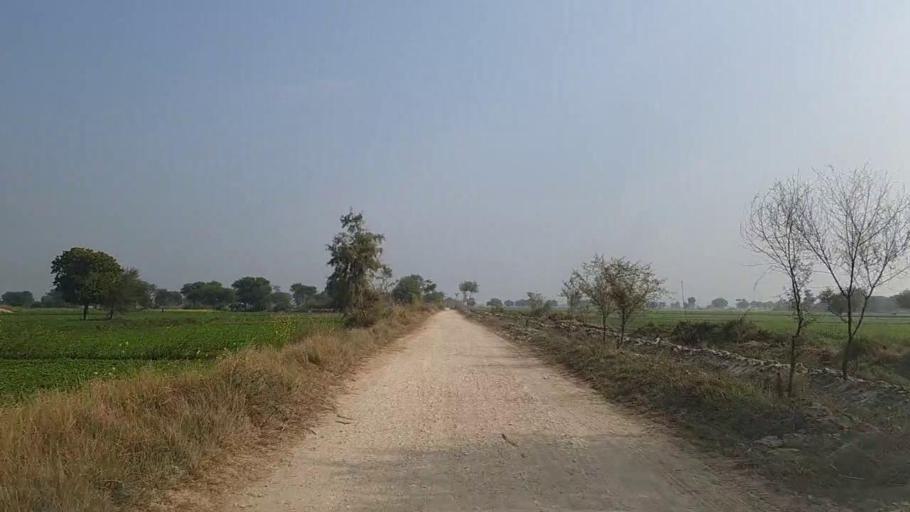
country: PK
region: Sindh
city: Nawabshah
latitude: 26.2892
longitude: 68.4434
